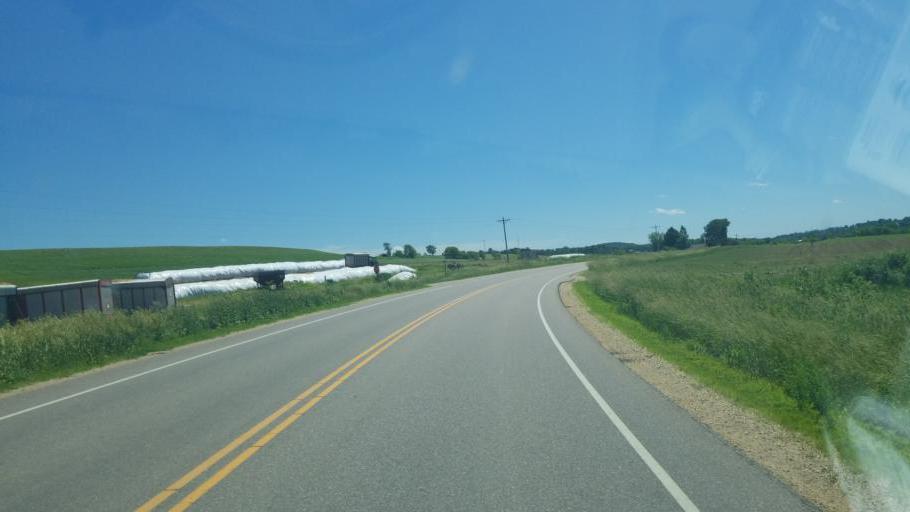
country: US
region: Wisconsin
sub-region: Juneau County
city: Elroy
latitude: 43.7718
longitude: -90.2721
